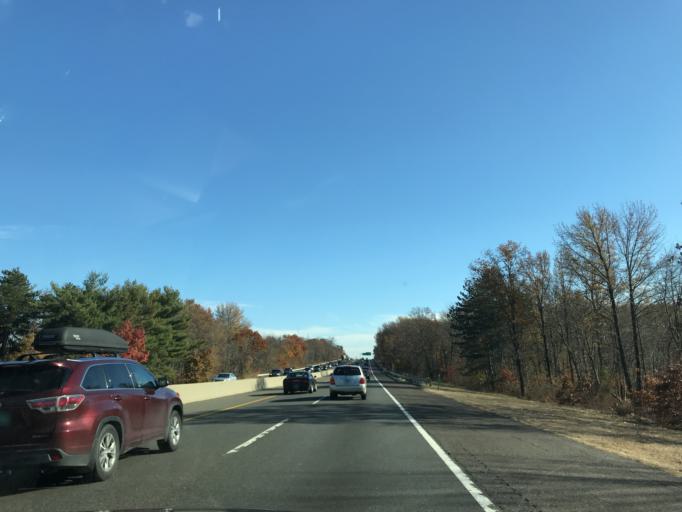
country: US
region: New Jersey
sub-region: Camden County
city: Bellmawr
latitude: 39.8572
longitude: -75.0884
